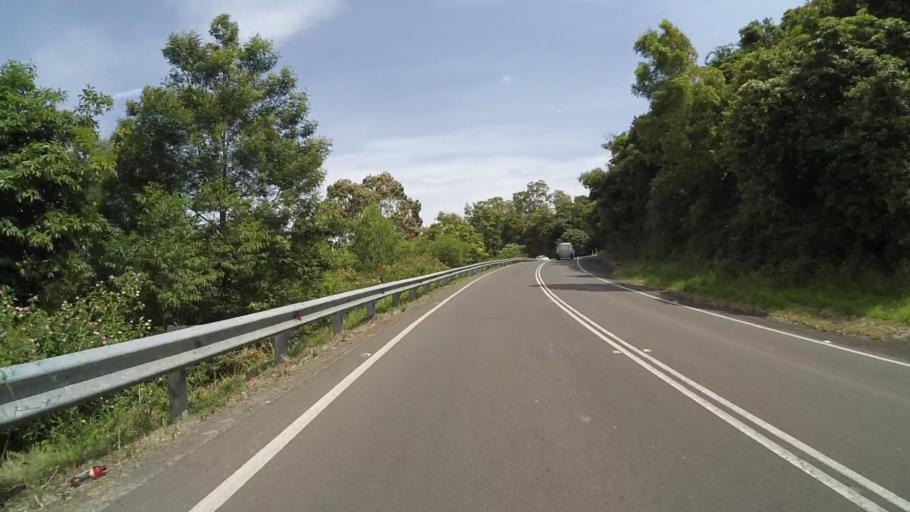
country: AU
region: New South Wales
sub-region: Shellharbour
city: Albion Park Rail
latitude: -34.5969
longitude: 150.7856
